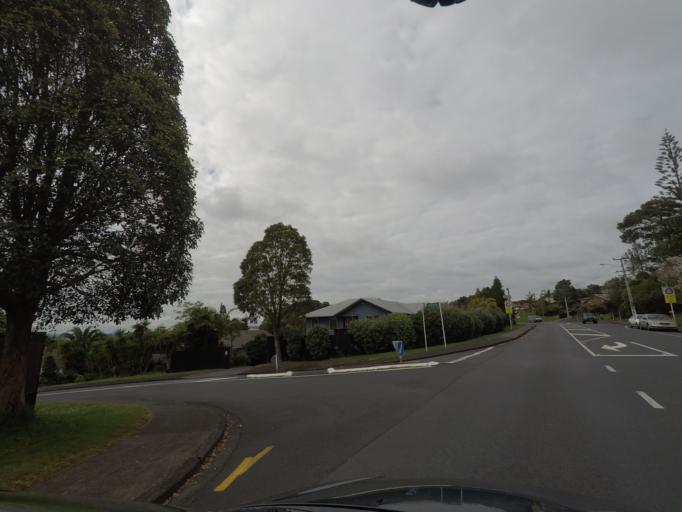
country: NZ
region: Auckland
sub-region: Auckland
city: Rosebank
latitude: -36.8517
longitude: 174.6100
